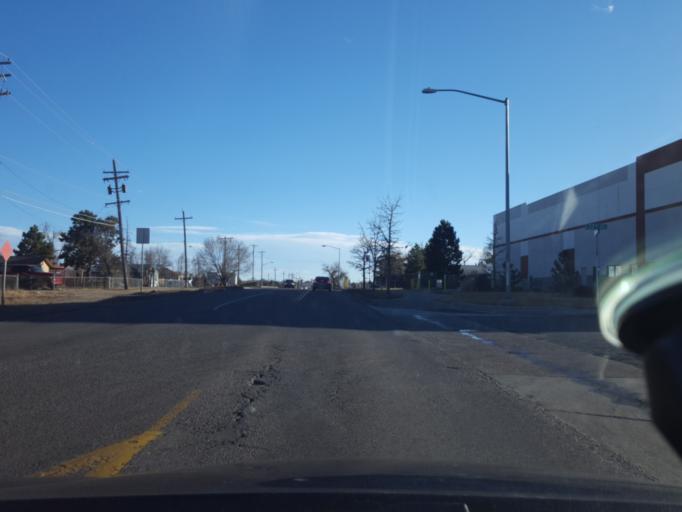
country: US
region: Colorado
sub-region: Adams County
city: Aurora
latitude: 39.7493
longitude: -104.7724
